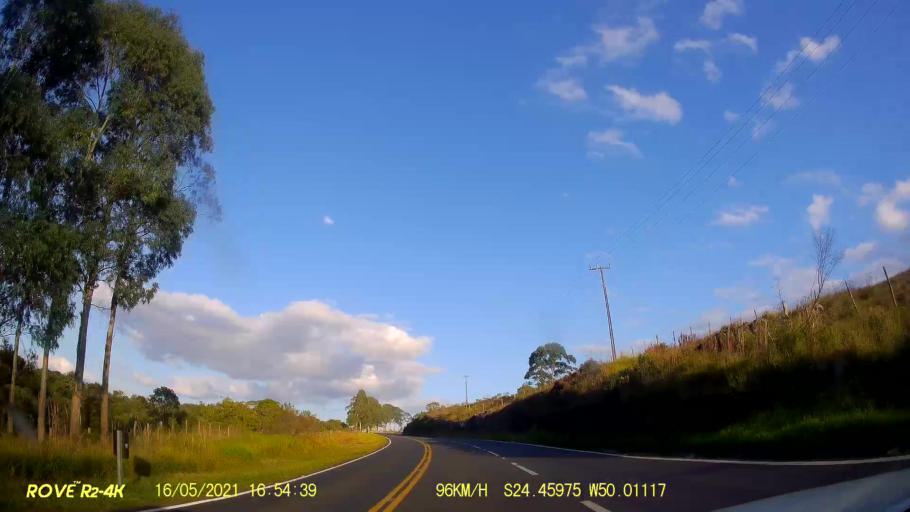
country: BR
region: Parana
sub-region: Pirai Do Sul
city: Pirai do Sul
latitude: -24.4597
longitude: -50.0112
